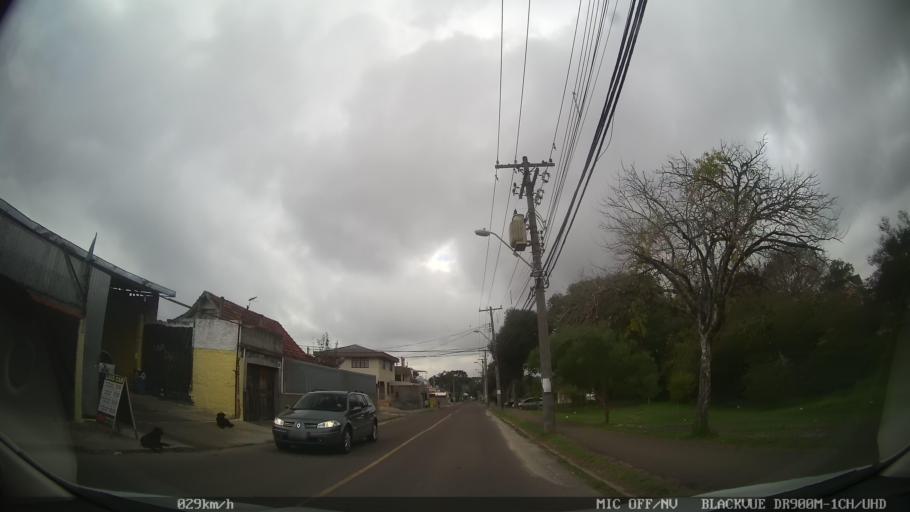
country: BR
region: Parana
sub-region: Curitiba
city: Curitiba
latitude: -25.3785
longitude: -49.2583
